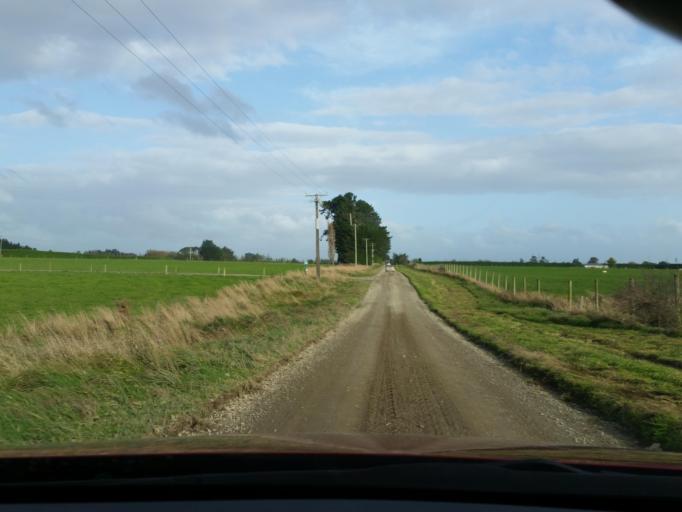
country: NZ
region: Southland
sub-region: Southland District
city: Winton
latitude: -46.2566
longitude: 168.3212
